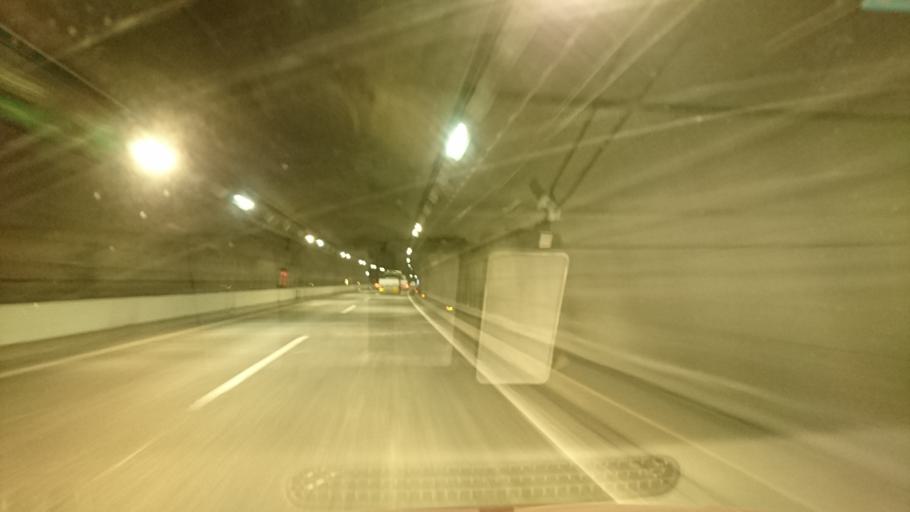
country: JP
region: Okayama
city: Okayama-shi
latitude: 34.6830
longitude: 133.8522
